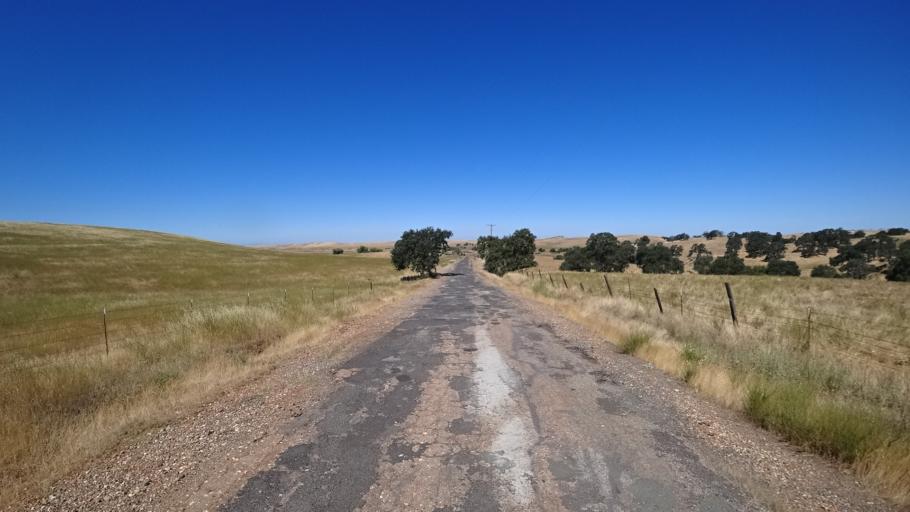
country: US
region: California
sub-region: Calaveras County
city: Rancho Calaveras
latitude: 38.0151
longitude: -120.8195
